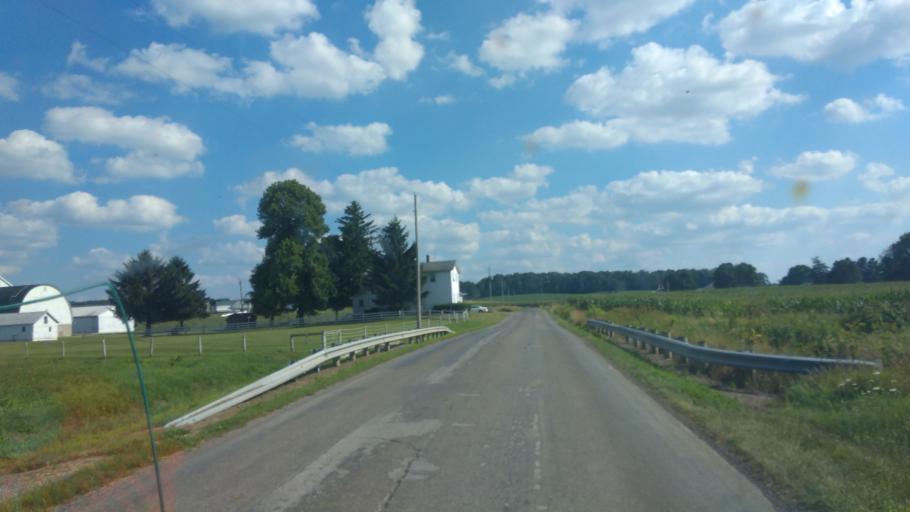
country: US
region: Ohio
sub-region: Wayne County
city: Apple Creek
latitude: 40.7297
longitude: -81.8438
